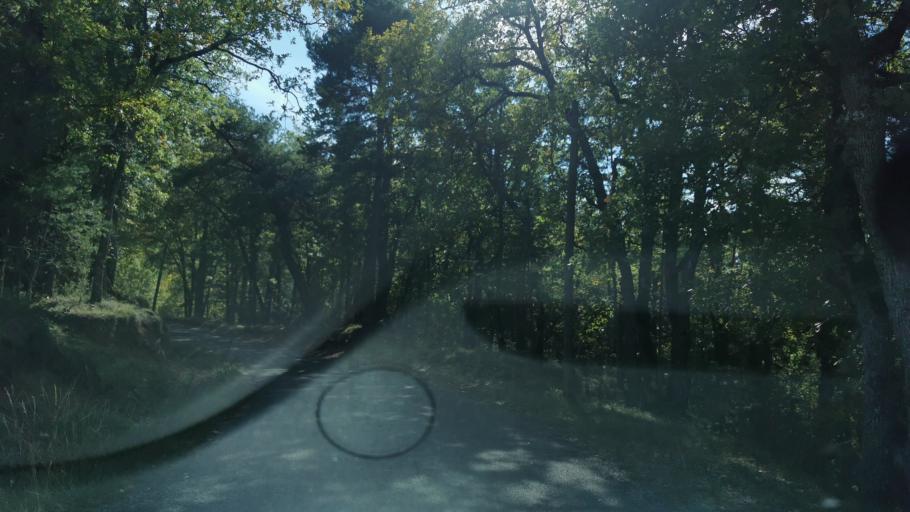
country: FR
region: Provence-Alpes-Cote d'Azur
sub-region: Departement des Alpes-de-Haute-Provence
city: Volonne
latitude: 44.1817
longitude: 6.0265
